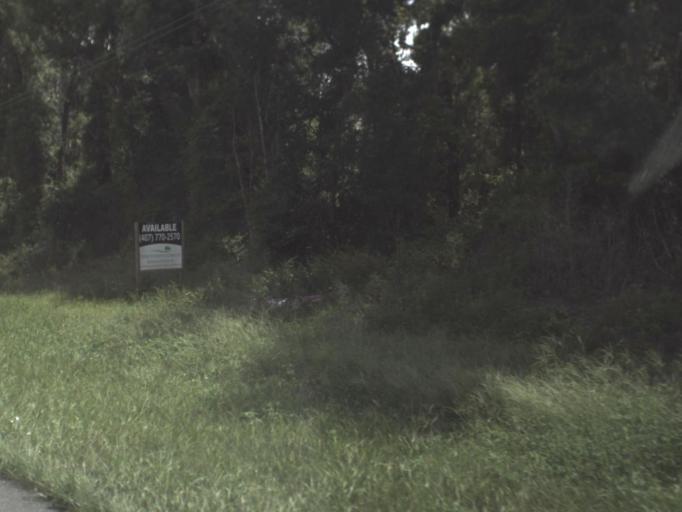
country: US
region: Florida
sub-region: Citrus County
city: Hernando
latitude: 28.9220
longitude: -82.3762
